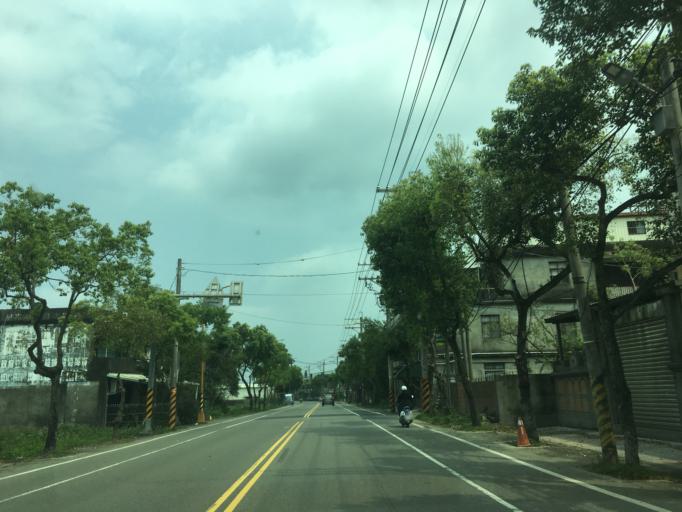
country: TW
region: Taiwan
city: Daxi
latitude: 24.8695
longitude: 121.2849
